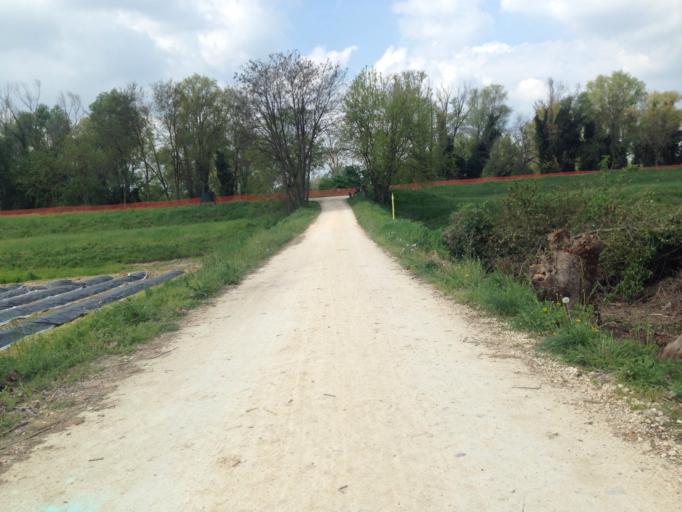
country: IT
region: Veneto
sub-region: Provincia di Verona
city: Campagnola
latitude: 45.3800
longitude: 11.0735
